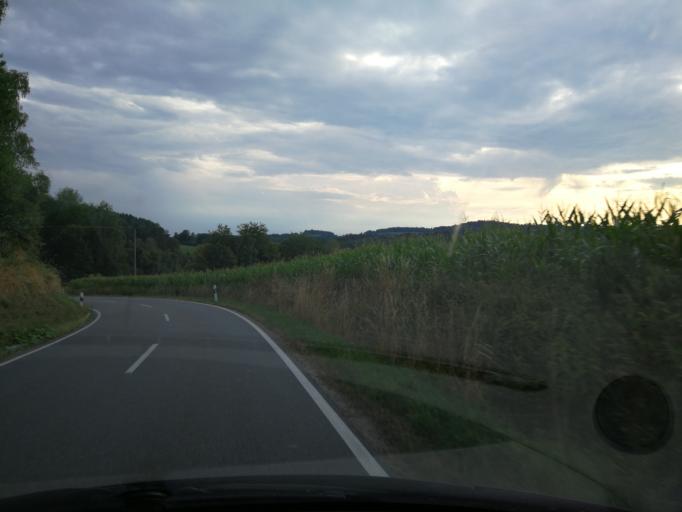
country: DE
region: Bavaria
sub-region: Lower Bavaria
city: Haibach
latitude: 49.0330
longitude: 12.7198
